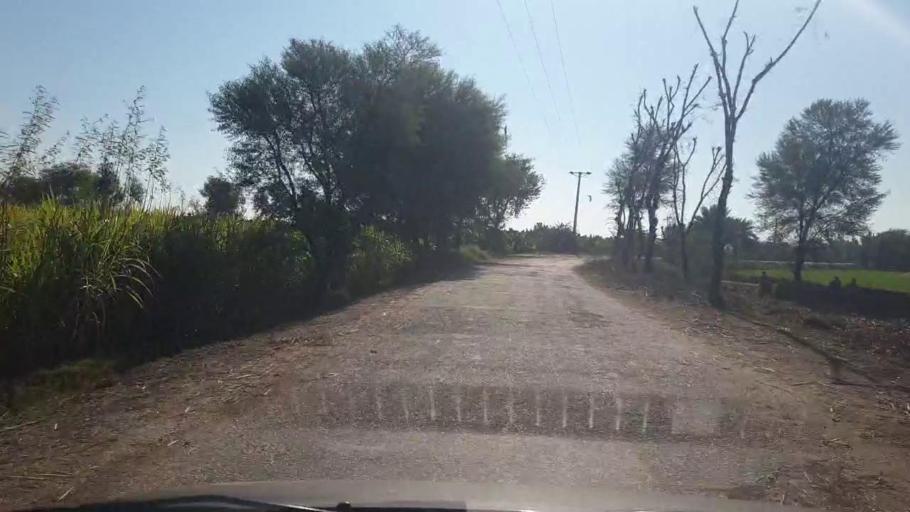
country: PK
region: Sindh
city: Bozdar
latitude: 27.2636
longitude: 68.6531
